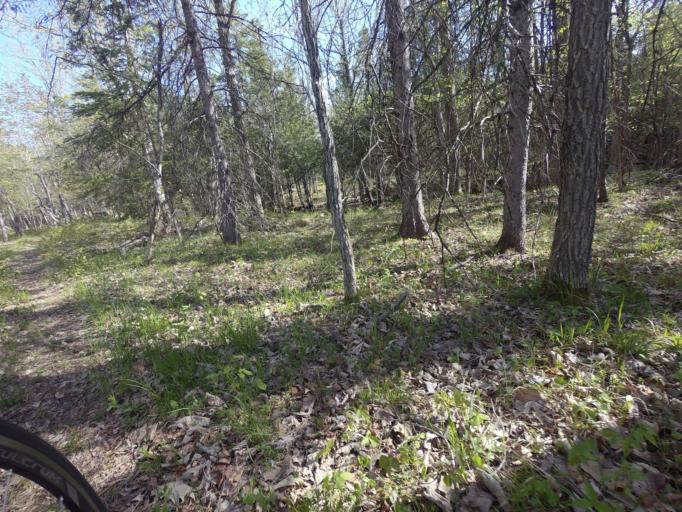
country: CA
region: Ontario
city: Arnprior
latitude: 45.4698
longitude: -76.2997
